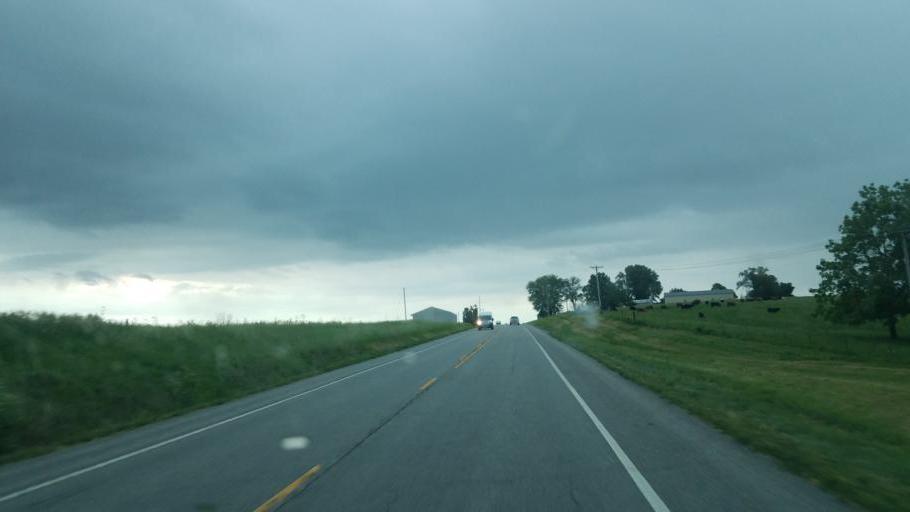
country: US
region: Missouri
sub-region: Cooper County
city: Boonville
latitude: 38.9163
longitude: -92.6850
